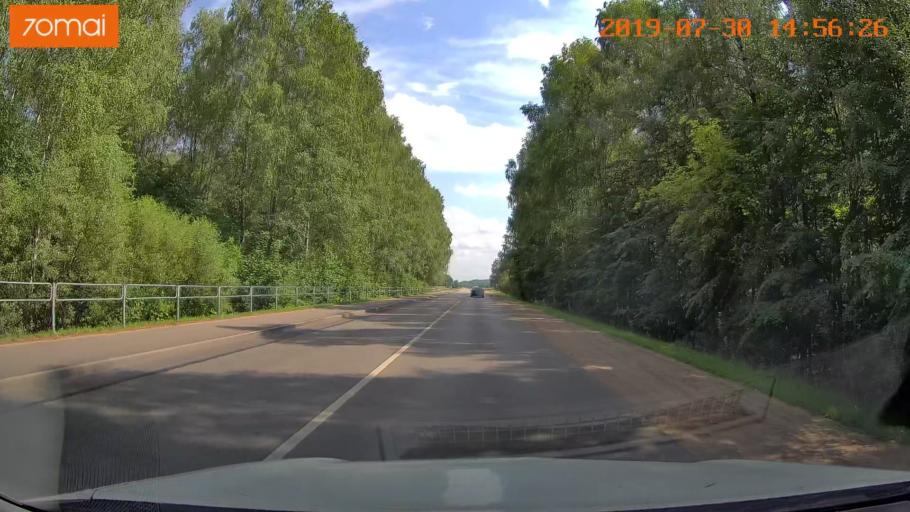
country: LT
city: Prienai
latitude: 54.6273
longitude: 23.9618
